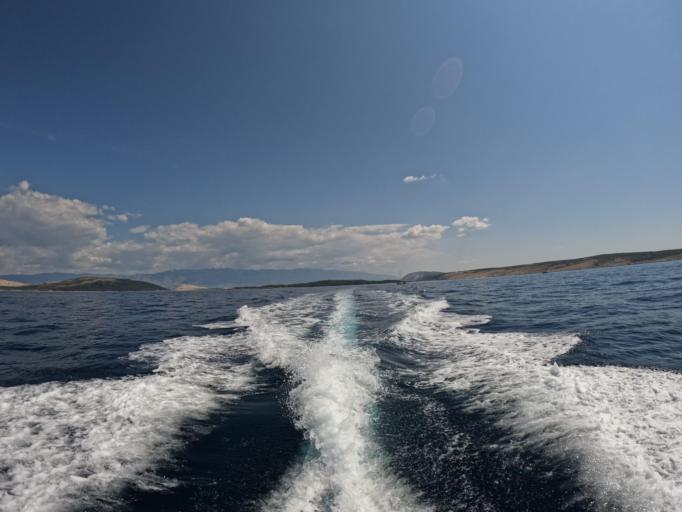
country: HR
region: Primorsko-Goranska
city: Lopar
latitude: 44.8609
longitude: 14.6943
